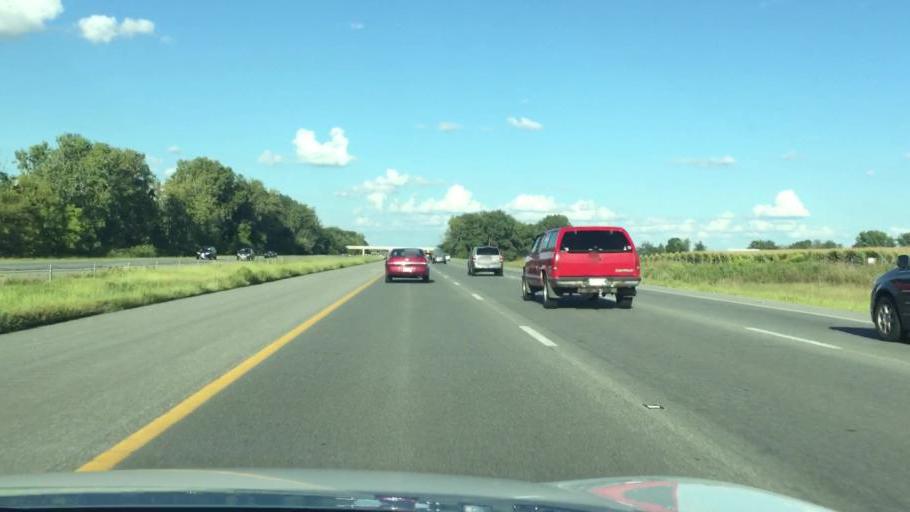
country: US
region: Ohio
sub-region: Madison County
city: Choctaw Lake
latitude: 39.9479
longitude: -83.4219
